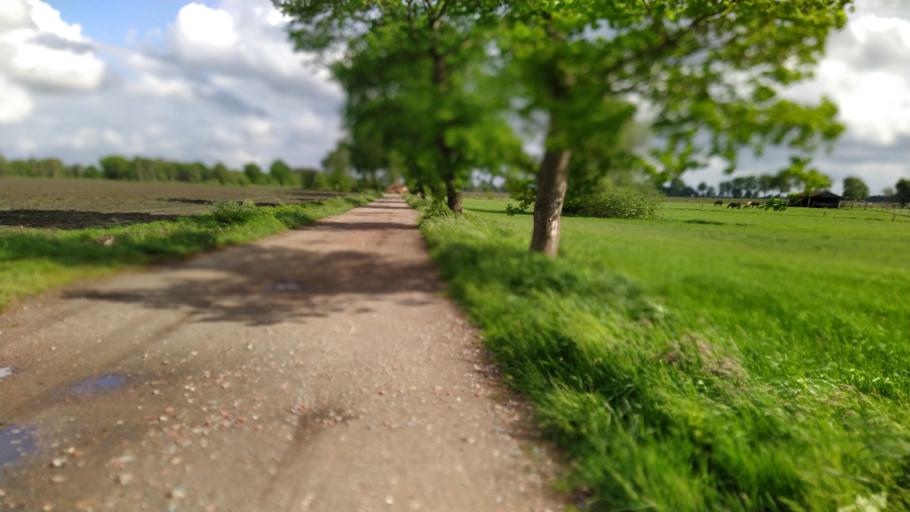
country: DE
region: Lower Saxony
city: Brest
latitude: 53.4627
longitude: 9.4015
